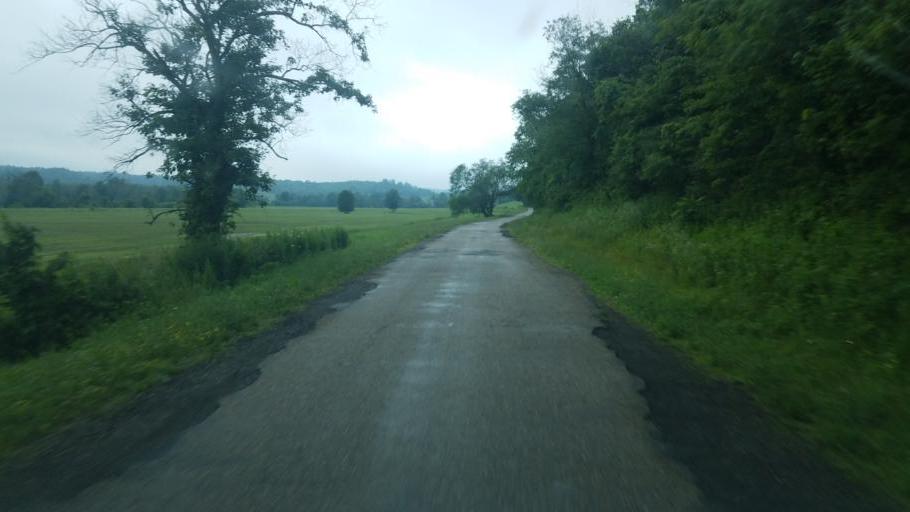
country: US
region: Ohio
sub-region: Tuscarawas County
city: Dennison
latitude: 40.3792
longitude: -81.2480
